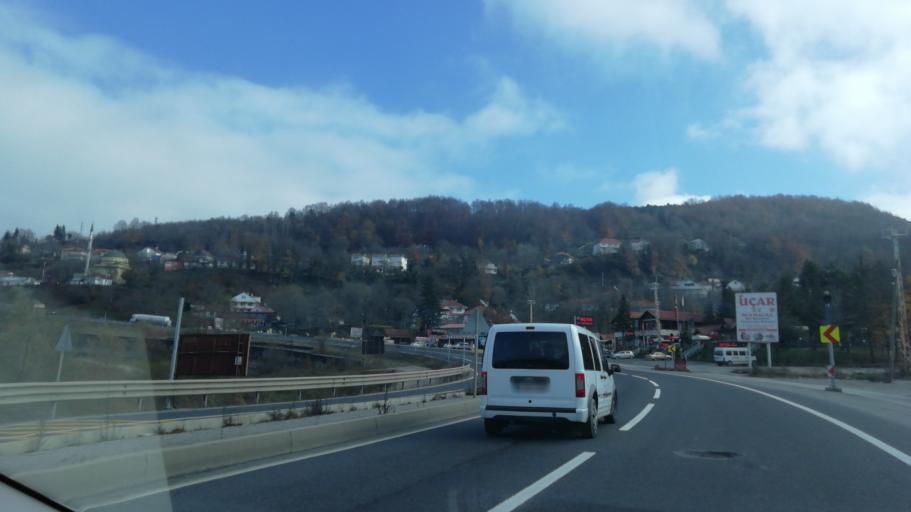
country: TR
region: Duzce
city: Kaynasli
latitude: 40.7471
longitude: 31.3808
